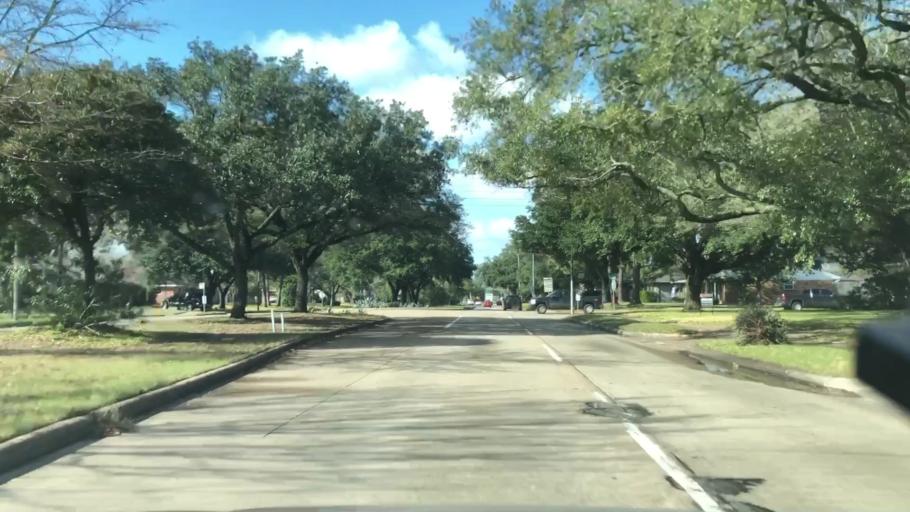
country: US
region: Texas
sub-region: Harris County
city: Bellaire
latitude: 29.6573
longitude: -95.4889
